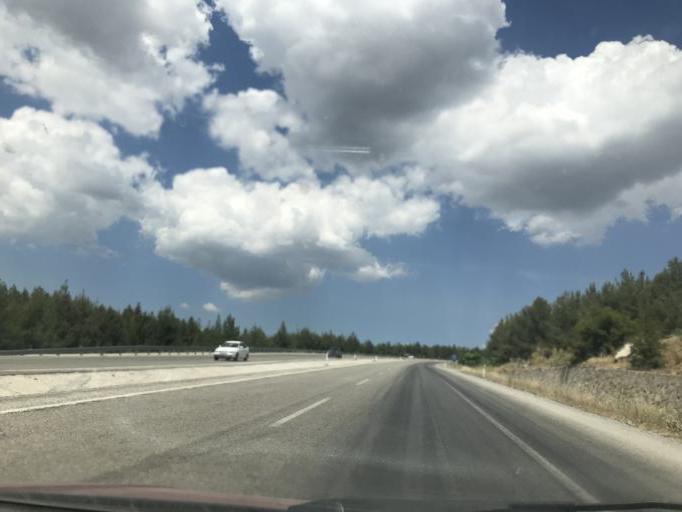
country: TR
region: Denizli
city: Tavas
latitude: 37.5783
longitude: 29.0889
